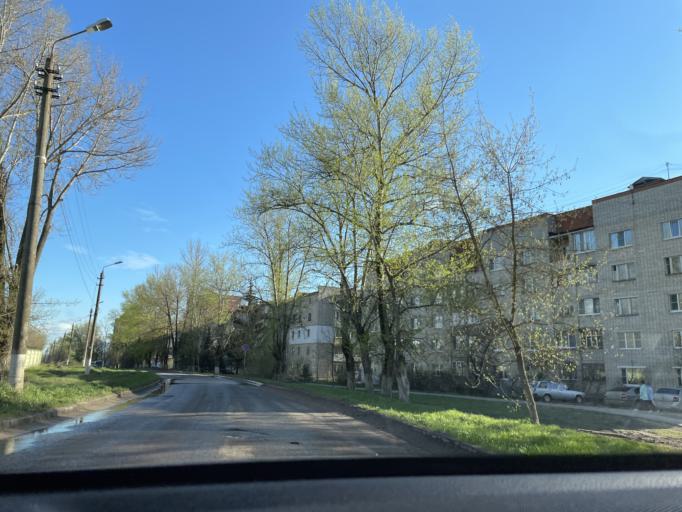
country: RU
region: Tula
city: Aleksin
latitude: 54.4928
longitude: 36.9851
